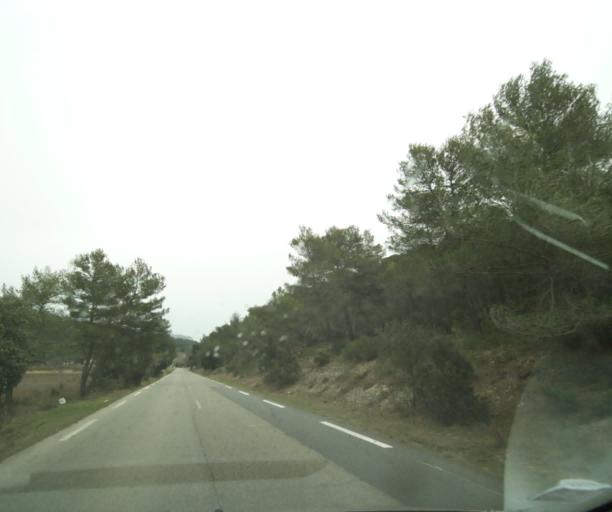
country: FR
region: Provence-Alpes-Cote d'Azur
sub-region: Departement des Bouches-du-Rhone
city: Saint-Marc-Jaumegarde
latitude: 43.5489
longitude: 5.5270
